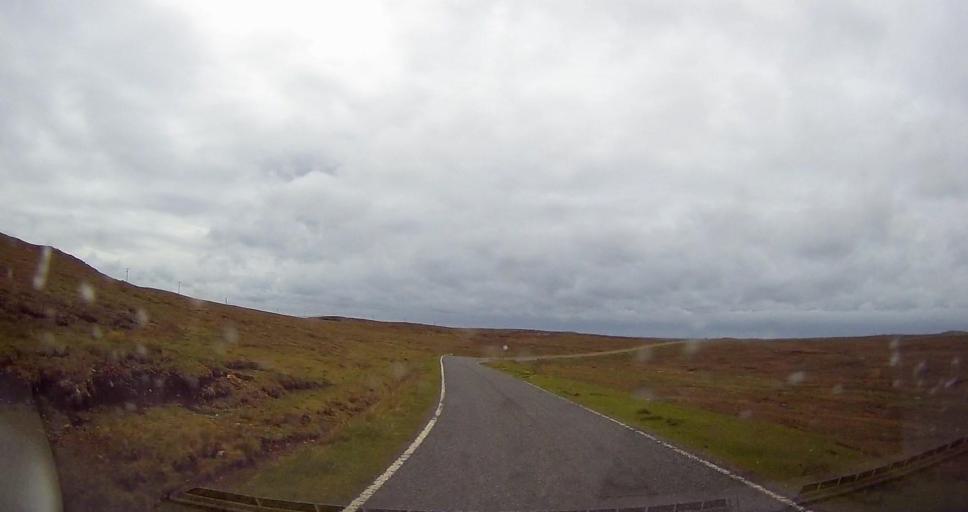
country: GB
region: Scotland
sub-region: Shetland Islands
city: Lerwick
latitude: 60.4933
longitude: -1.5701
